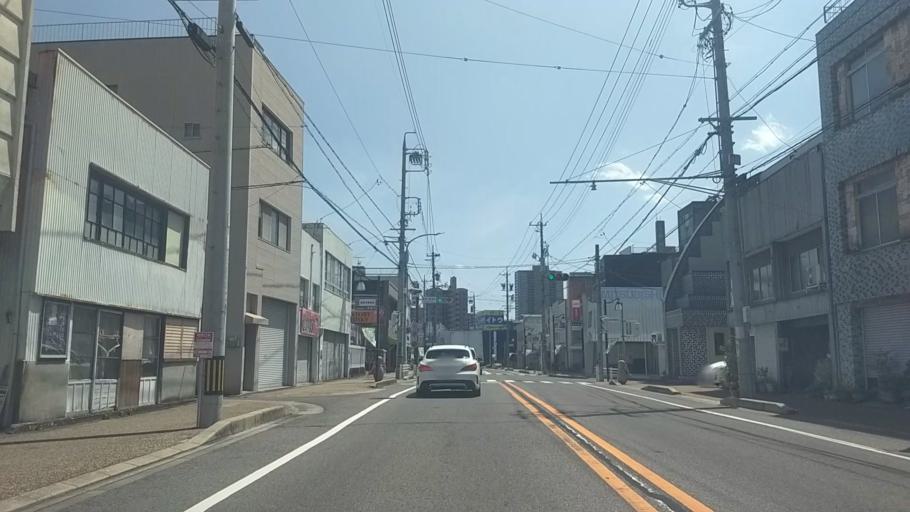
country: JP
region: Aichi
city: Okazaki
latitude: 34.9657
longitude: 137.1630
